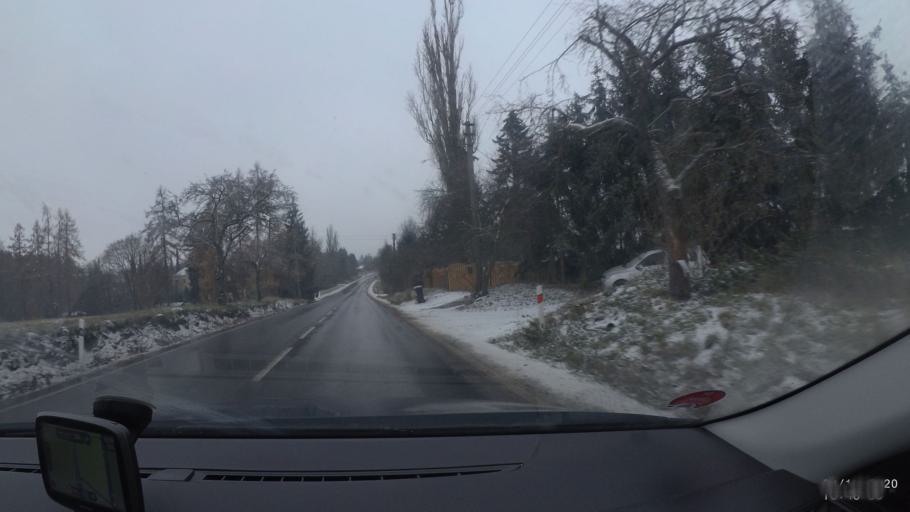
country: CZ
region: Central Bohemia
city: Nove Straseci
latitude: 50.1655
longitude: 13.8984
